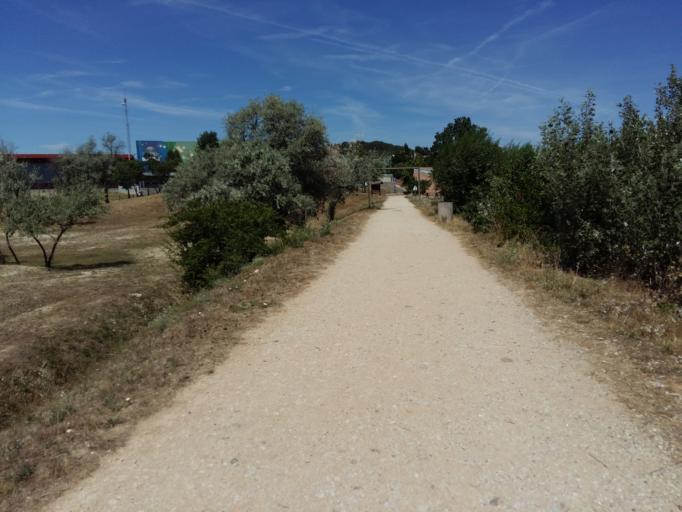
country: FR
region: Provence-Alpes-Cote d'Azur
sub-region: Departement du Vaucluse
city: Apt
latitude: 43.8906
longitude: 5.3780
